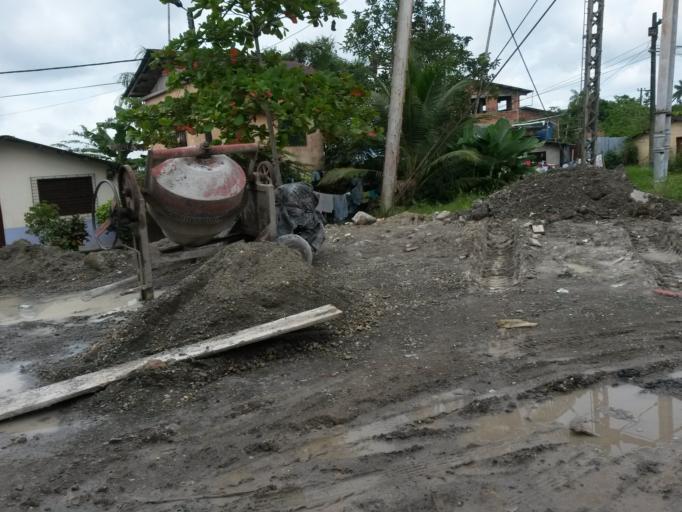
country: CO
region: Cauca
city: Guapi
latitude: 2.5720
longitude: -77.8900
